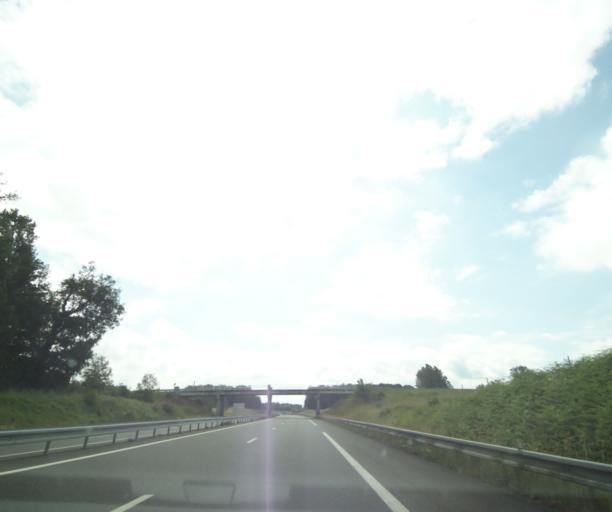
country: FR
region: Pays de la Loire
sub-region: Departement de Maine-et-Loire
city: Brion
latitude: 47.4317
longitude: -0.1606
